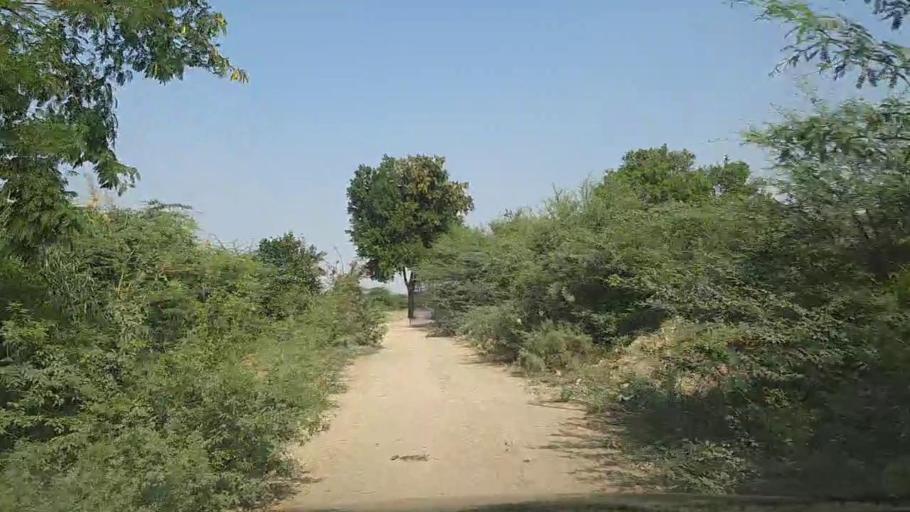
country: PK
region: Sindh
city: Mirpur Sakro
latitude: 24.6188
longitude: 67.7793
